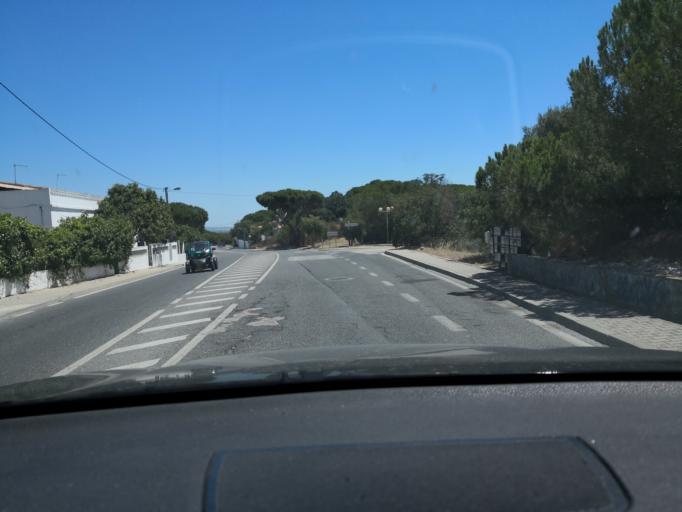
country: PT
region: Faro
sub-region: Albufeira
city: Ferreiras
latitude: 37.1084
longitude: -8.2058
